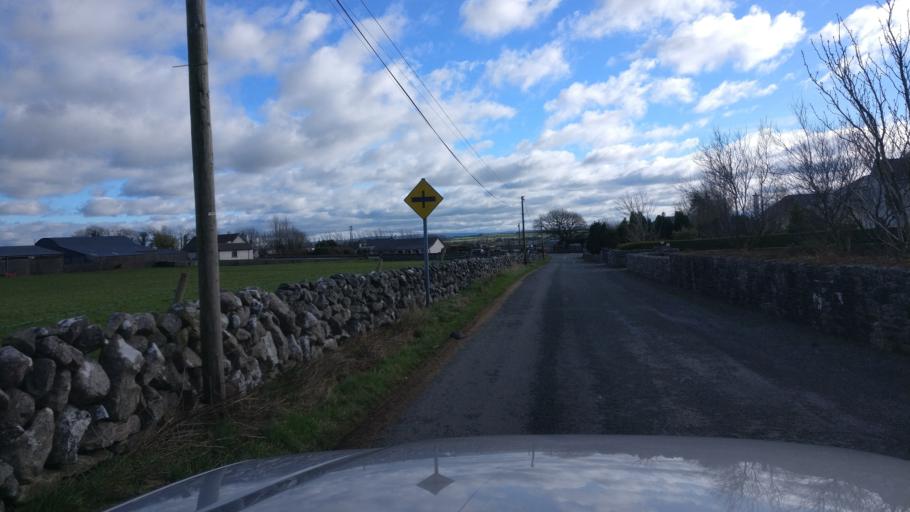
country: IE
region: Connaught
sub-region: County Galway
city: Oranmore
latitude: 53.2778
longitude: -8.8907
